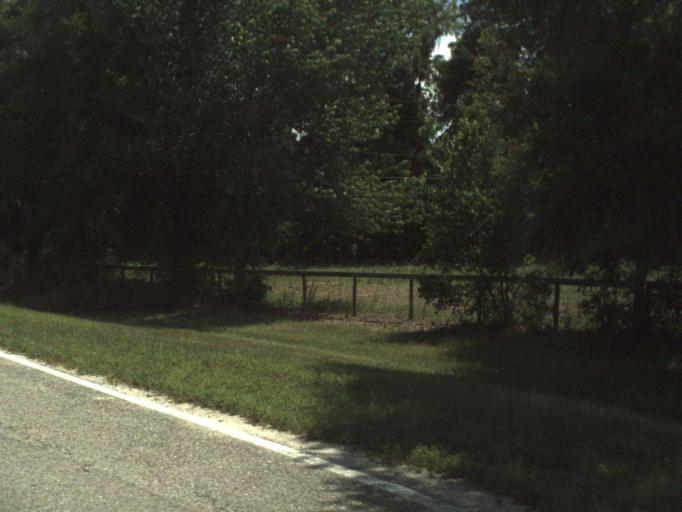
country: US
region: Florida
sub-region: Marion County
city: Citra
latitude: 29.3677
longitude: -82.1707
